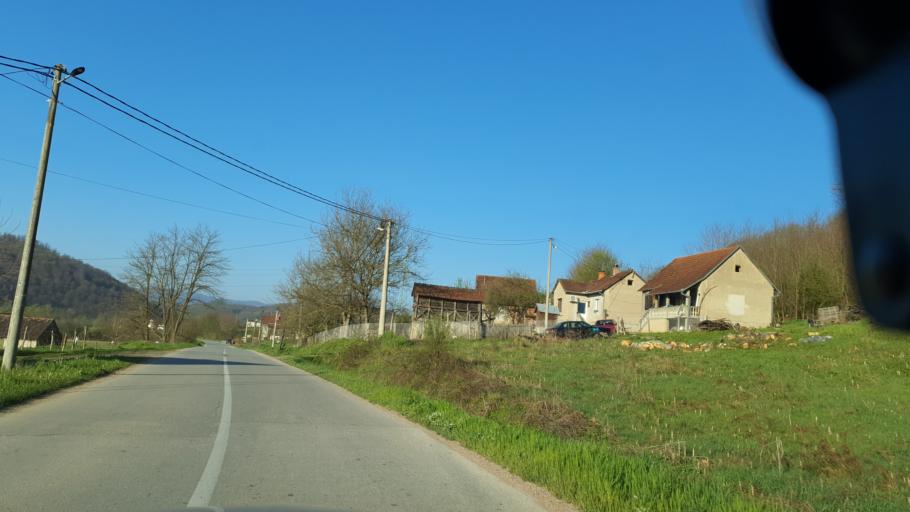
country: RS
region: Central Serbia
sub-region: Kolubarski Okrug
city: Osecina
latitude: 44.3829
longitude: 19.5552
